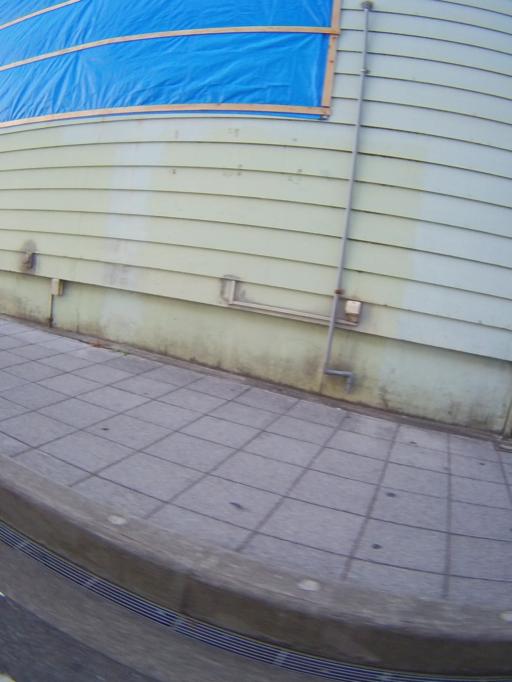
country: JP
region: Hyogo
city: Amagasaki
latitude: 34.6845
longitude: 135.4527
